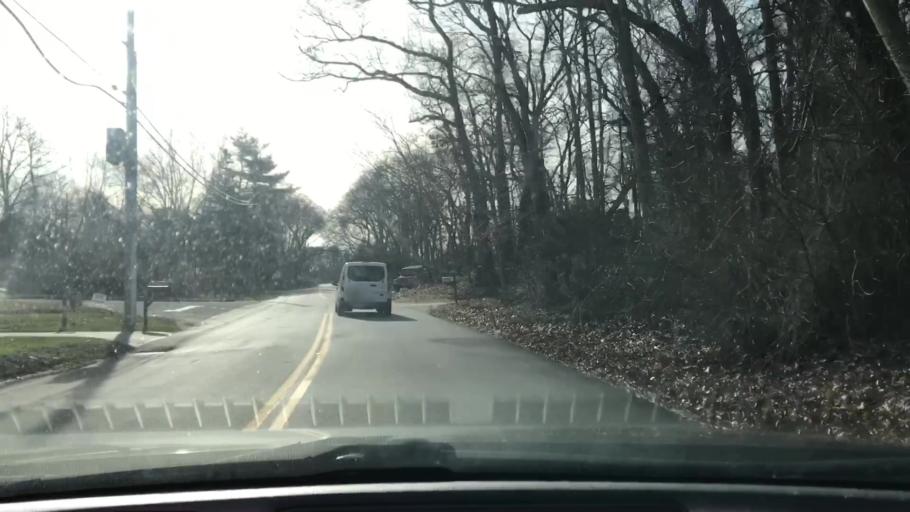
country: US
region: New York
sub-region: Suffolk County
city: Aquebogue
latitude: 40.9501
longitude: -72.6205
